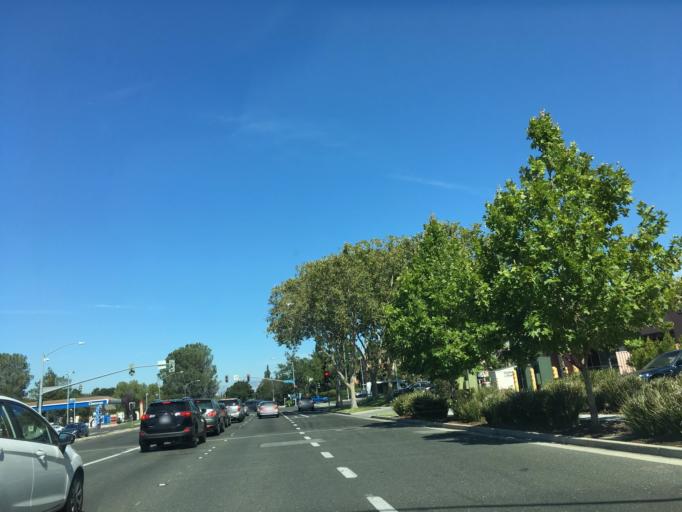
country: US
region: California
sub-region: Santa Clara County
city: Cupertino
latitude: 37.3375
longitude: -122.0335
